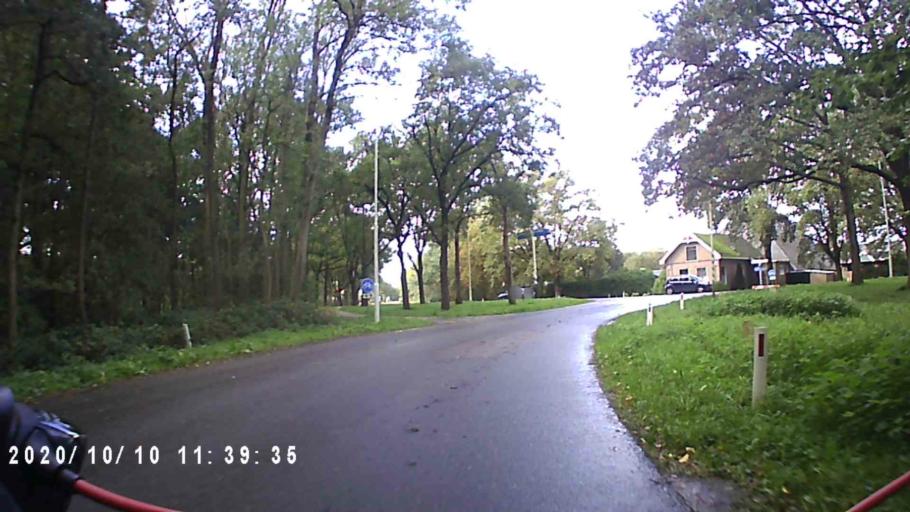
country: NL
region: Friesland
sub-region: Gemeente Smallingerland
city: Drachten
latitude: 53.0686
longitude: 6.1061
